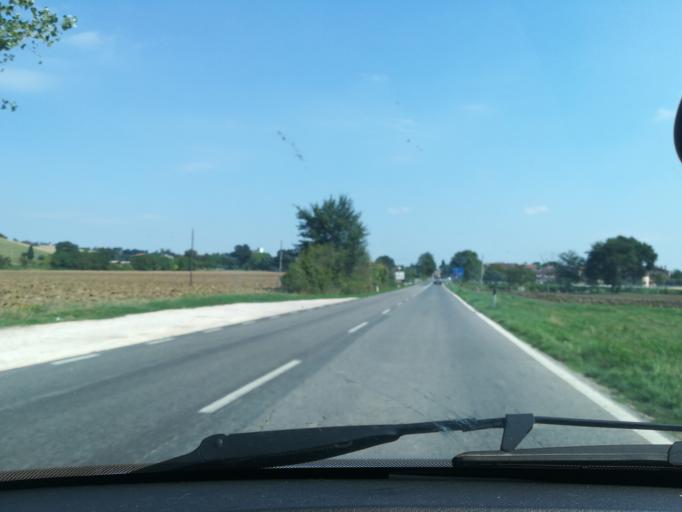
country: IT
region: The Marches
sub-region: Provincia di Macerata
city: Pollenza
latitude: 43.2373
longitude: 13.3632
